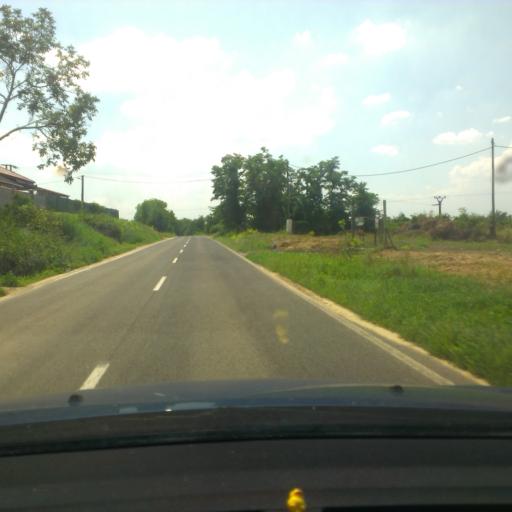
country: SK
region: Trnavsky
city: Hlohovec
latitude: 48.4835
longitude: 17.8082
